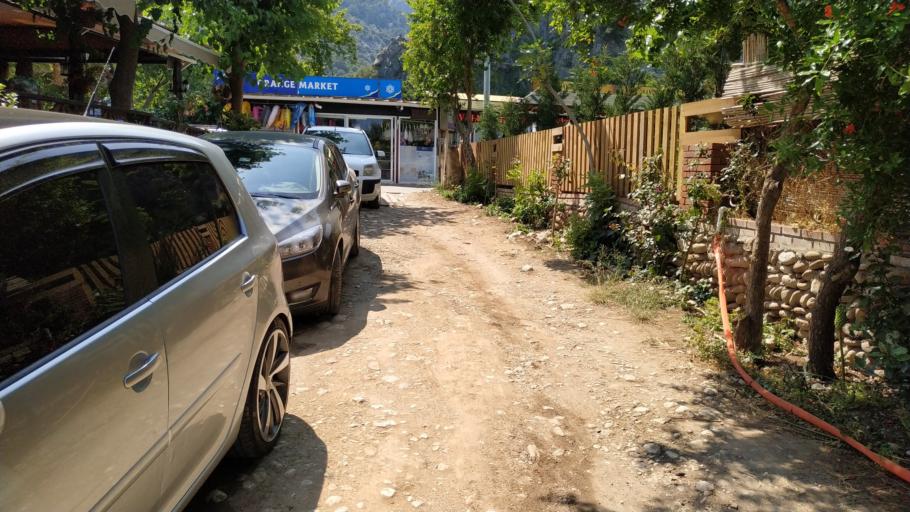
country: TR
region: Antalya
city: Tekirova
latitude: 36.4045
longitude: 30.4743
